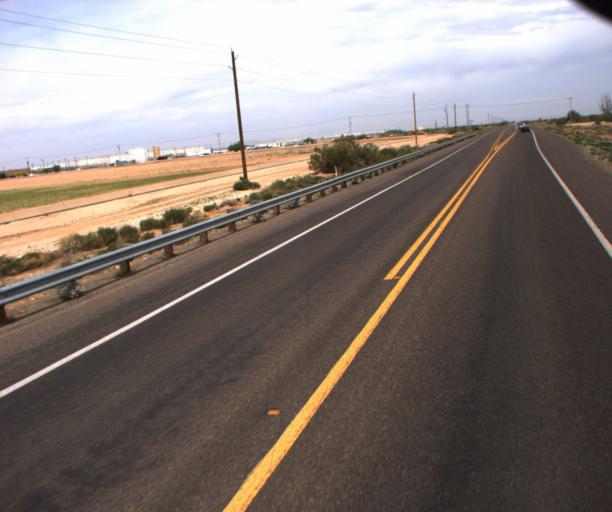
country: US
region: Arizona
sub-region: Pinal County
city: Eloy
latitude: 32.8041
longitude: -111.5154
